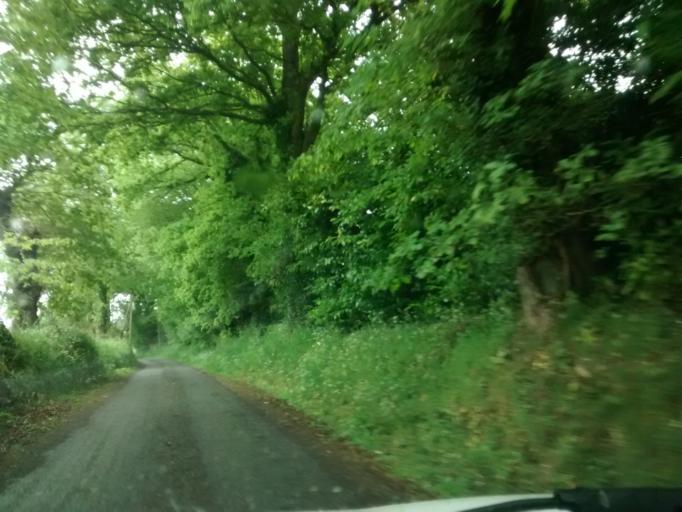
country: FR
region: Brittany
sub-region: Departement d'Ille-et-Vilaine
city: Acigne
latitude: 48.1123
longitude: -1.5667
